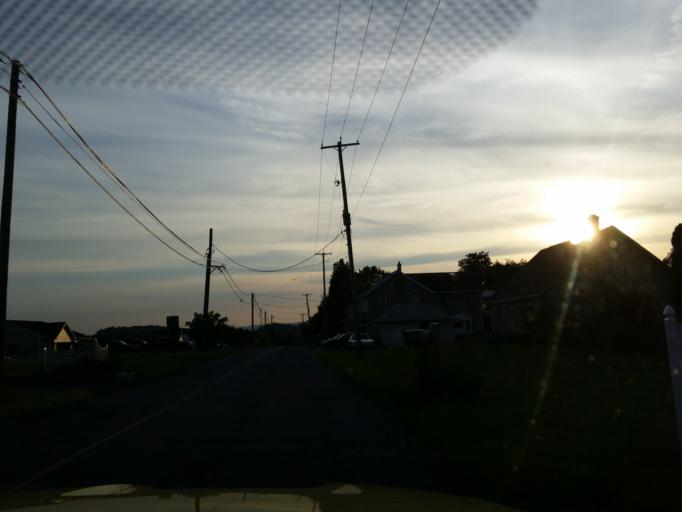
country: US
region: Pennsylvania
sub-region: Lebanon County
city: Fredericksburg
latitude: 40.4481
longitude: -76.3786
